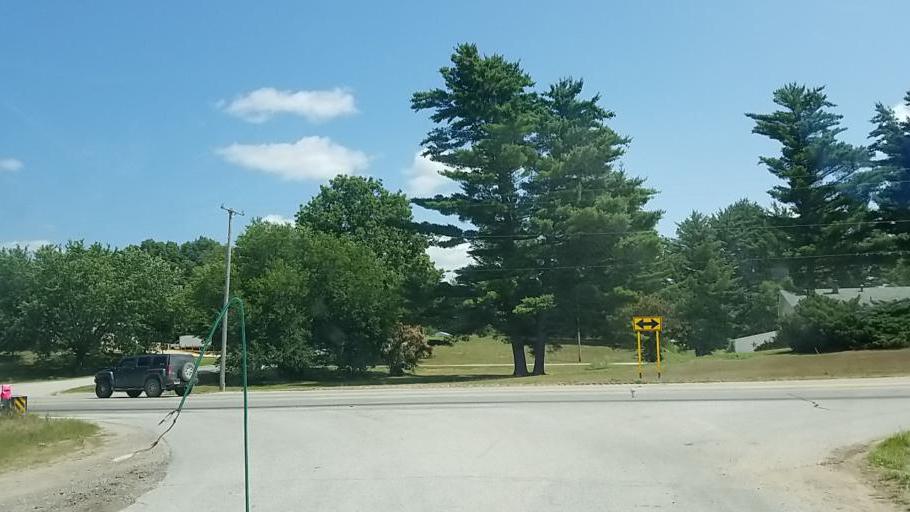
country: US
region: Michigan
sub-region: Newaygo County
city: Fremont
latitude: 43.4814
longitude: -86.0399
